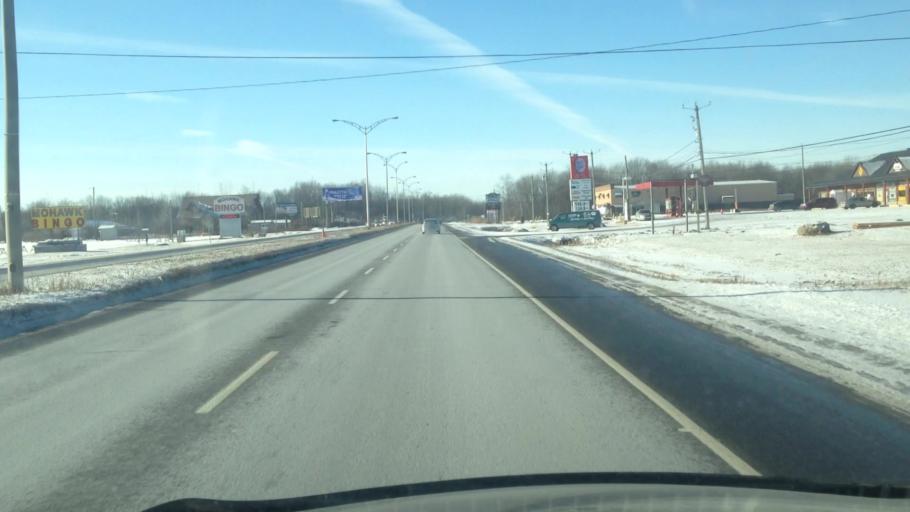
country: CA
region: Quebec
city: Montreal-Ouest
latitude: 45.4005
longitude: -73.6804
